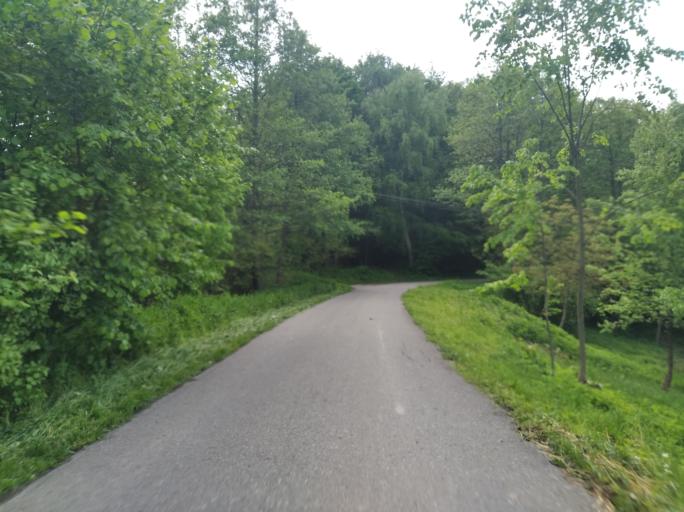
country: PL
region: Subcarpathian Voivodeship
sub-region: Powiat strzyzowski
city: Czudec
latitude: 49.9244
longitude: 21.8342
